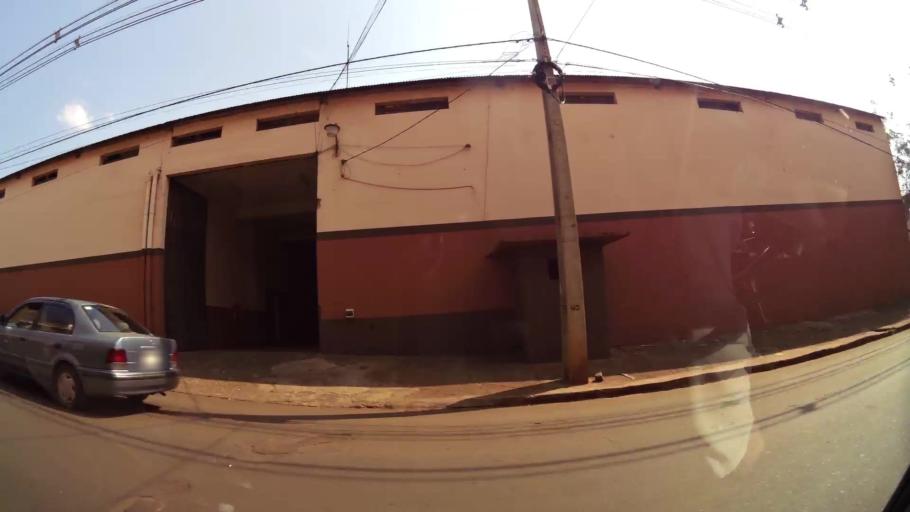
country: PY
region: Alto Parana
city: Ciudad del Este
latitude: -25.5068
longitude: -54.6238
